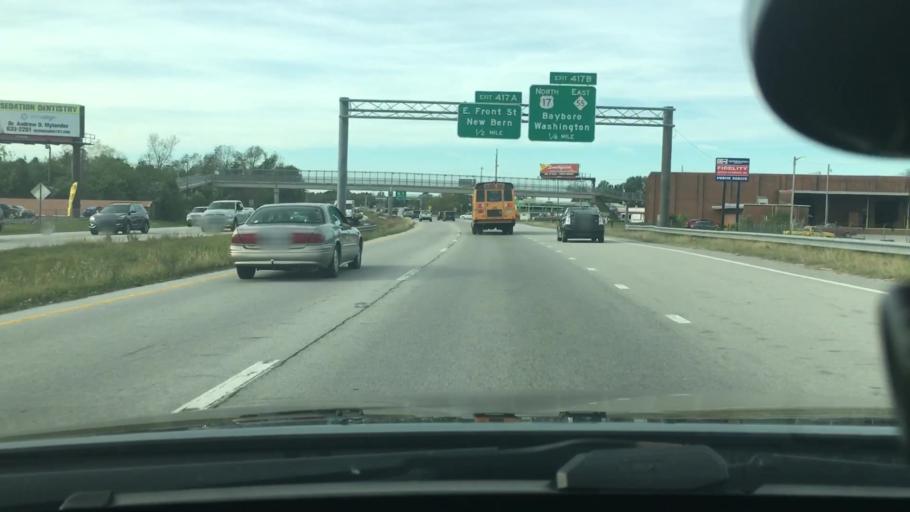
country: US
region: North Carolina
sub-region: Craven County
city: James City
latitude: 35.0860
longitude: -77.0326
